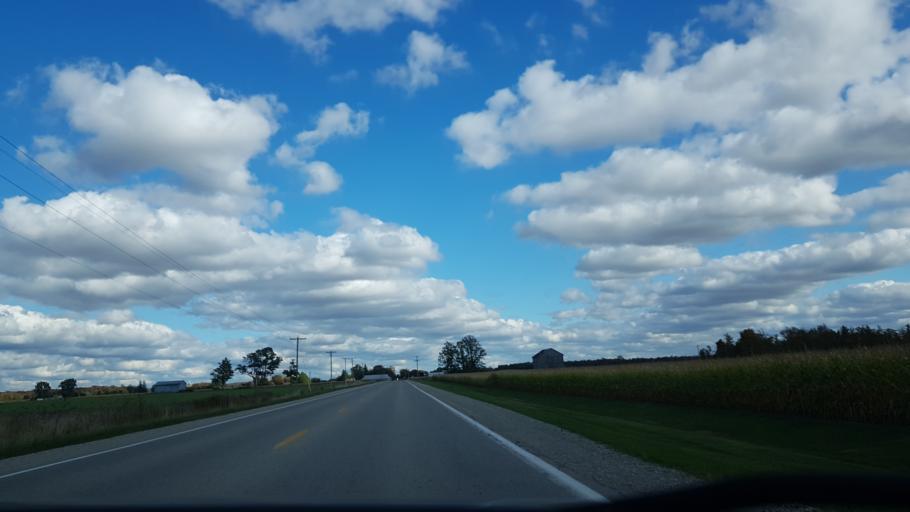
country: CA
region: Ontario
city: Lambton Shores
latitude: 43.2413
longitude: -81.7304
